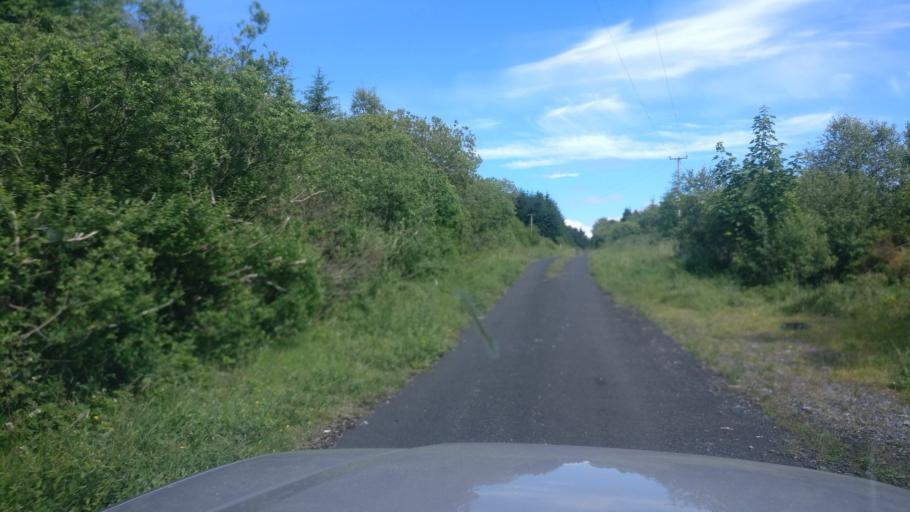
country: IE
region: Connaught
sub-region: County Galway
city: Gort
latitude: 53.0639
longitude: -8.6929
